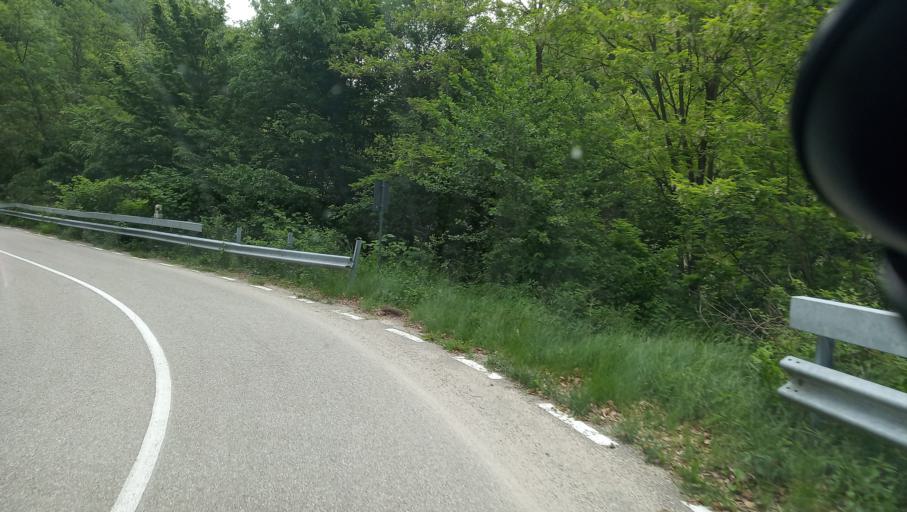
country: RO
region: Caras-Severin
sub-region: Comuna Slatina-Timis
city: Slatina-Timis
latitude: 45.2586
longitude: 22.2455
